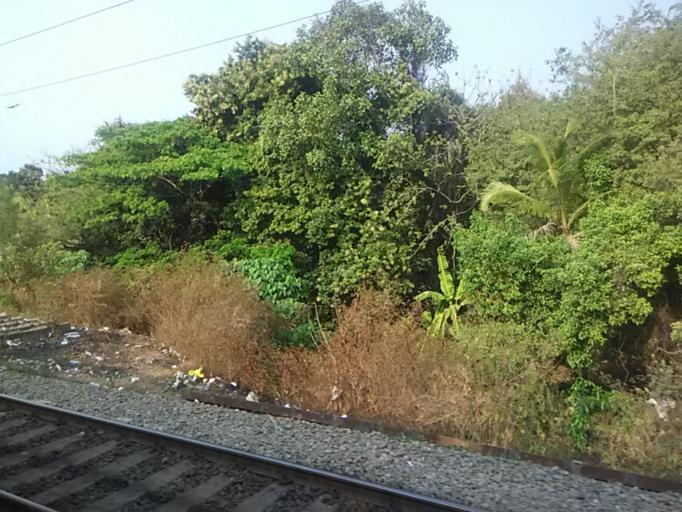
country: IN
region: Kerala
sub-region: Malappuram
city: Pariyapuram
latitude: 11.0414
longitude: 75.8632
